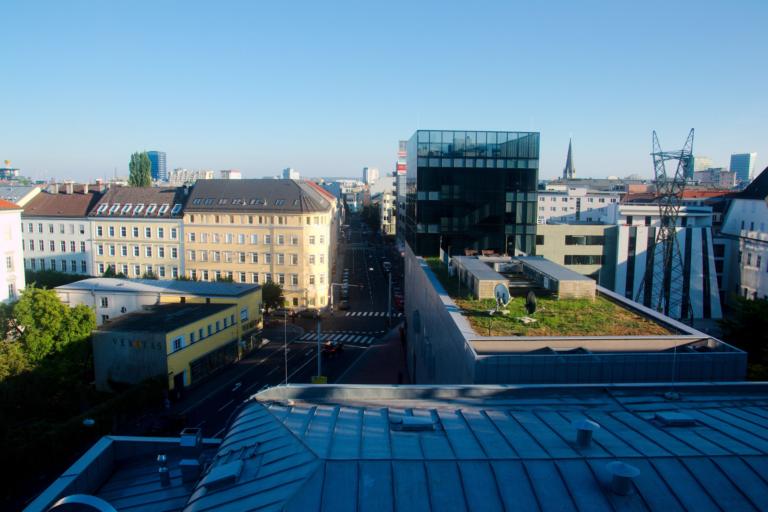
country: AT
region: Upper Austria
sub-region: Linz Stadt
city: Linz
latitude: 48.3031
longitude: 14.2909
